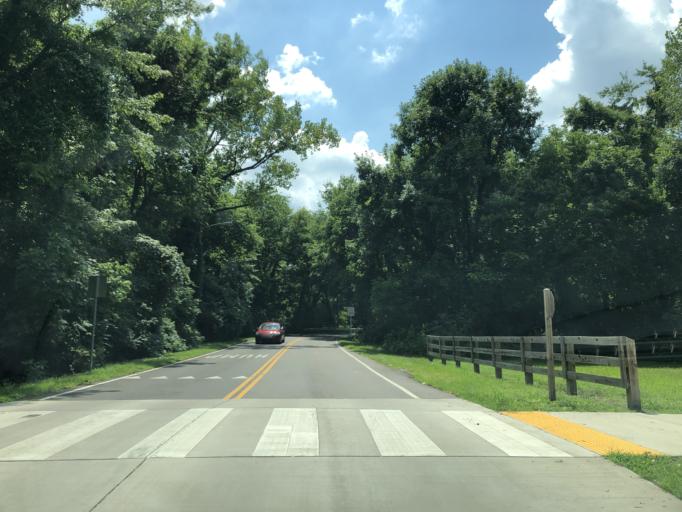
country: US
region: Tennessee
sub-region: Davidson County
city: Oak Hill
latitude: 36.1179
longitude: -86.7241
